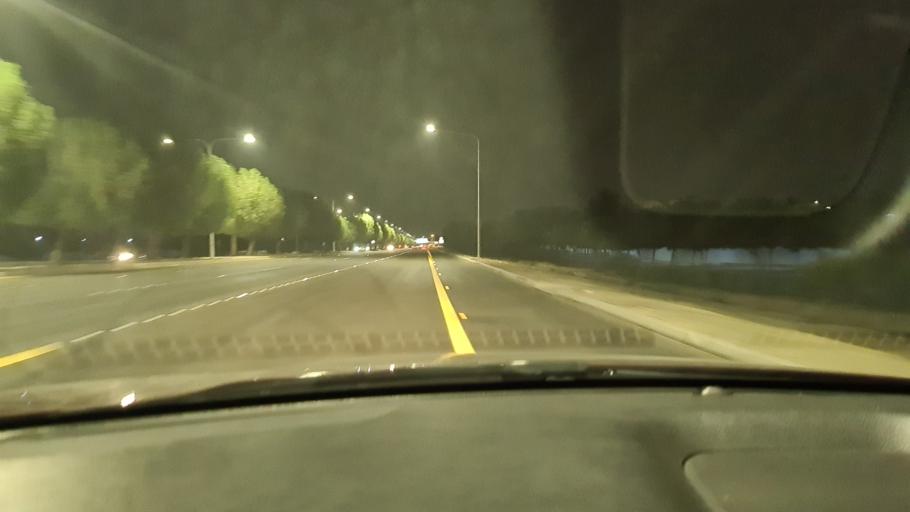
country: SA
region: Eastern Province
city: Al Jubayl
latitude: 27.1239
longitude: 49.5427
